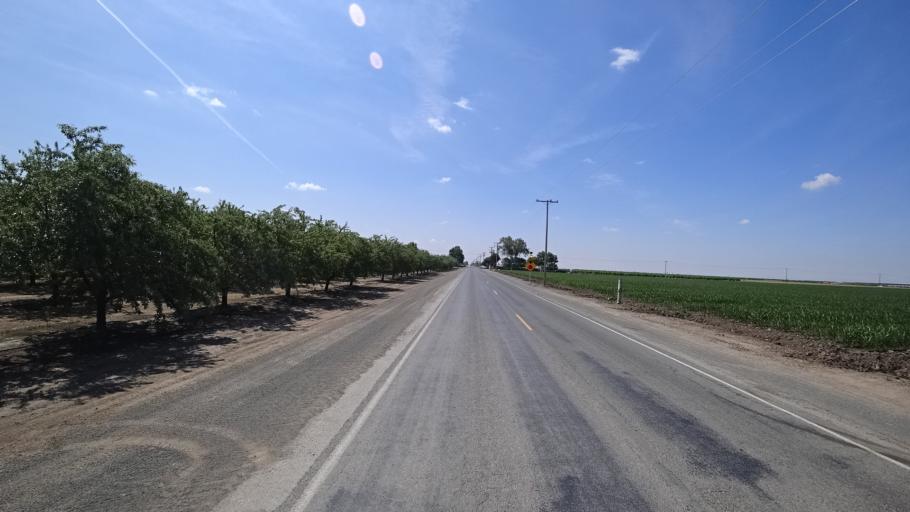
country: US
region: California
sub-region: Tulare County
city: Goshen
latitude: 36.2709
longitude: -119.4924
